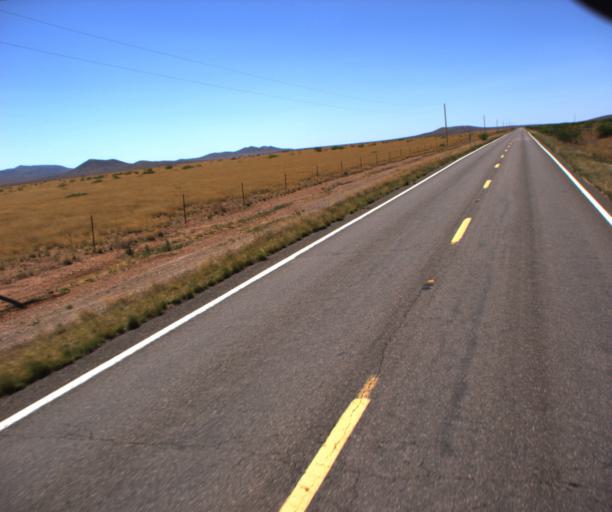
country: US
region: Arizona
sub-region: Cochise County
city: Douglas
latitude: 31.6699
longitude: -109.1472
